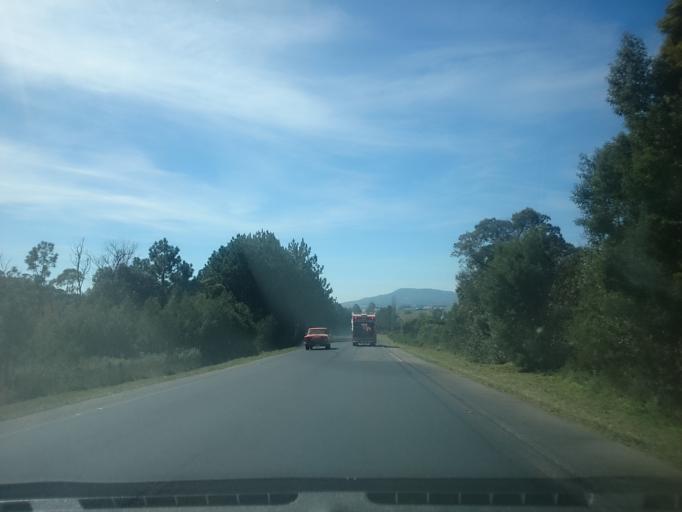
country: BR
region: Santa Catarina
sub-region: Lages
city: Lages
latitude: -27.7755
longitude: -50.2132
